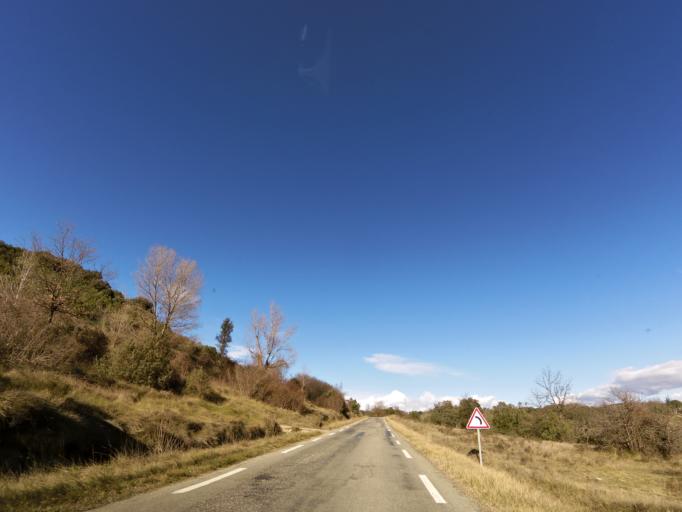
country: FR
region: Languedoc-Roussillon
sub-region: Departement du Gard
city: Sauve
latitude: 43.9714
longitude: 3.9485
